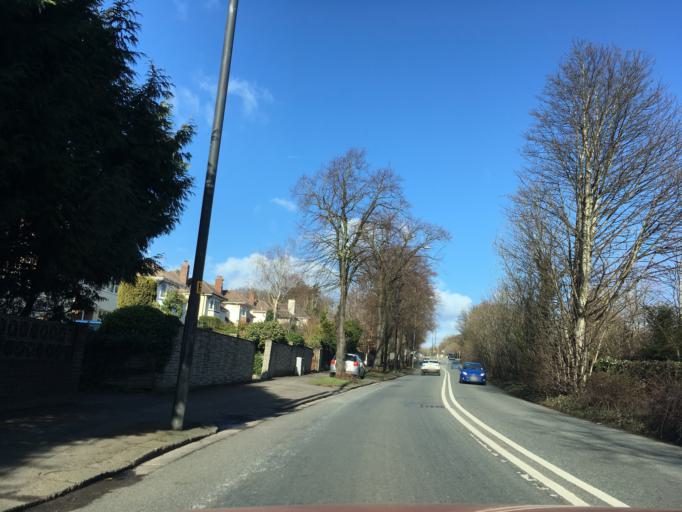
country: GB
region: England
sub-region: Bristol
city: Bristol
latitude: 51.5003
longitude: -2.6167
